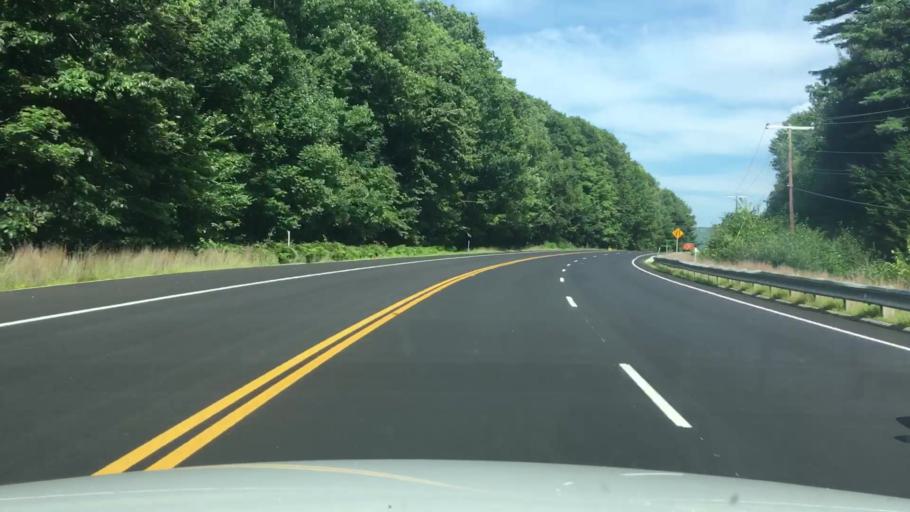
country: US
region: New Hampshire
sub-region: Belknap County
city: Gilford
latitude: 43.5421
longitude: -71.4229
